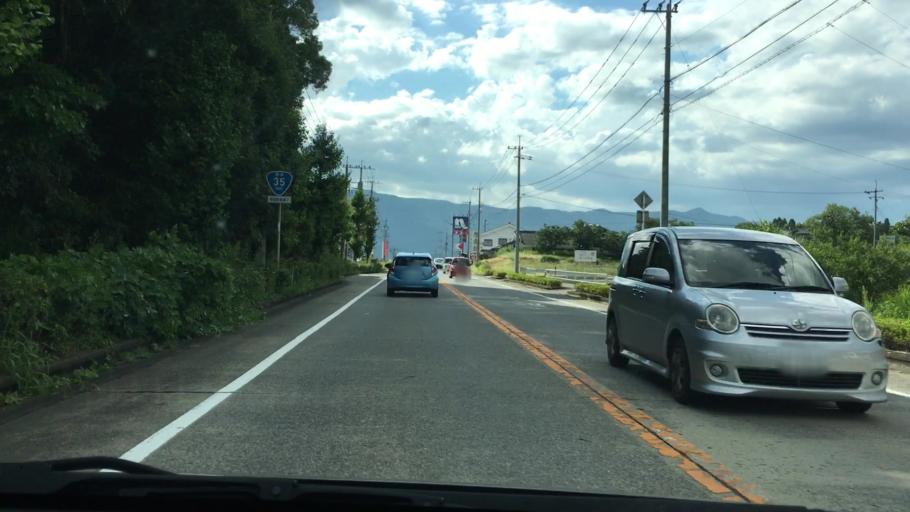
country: JP
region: Saga Prefecture
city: Imaricho-ko
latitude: 33.1828
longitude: 129.8752
